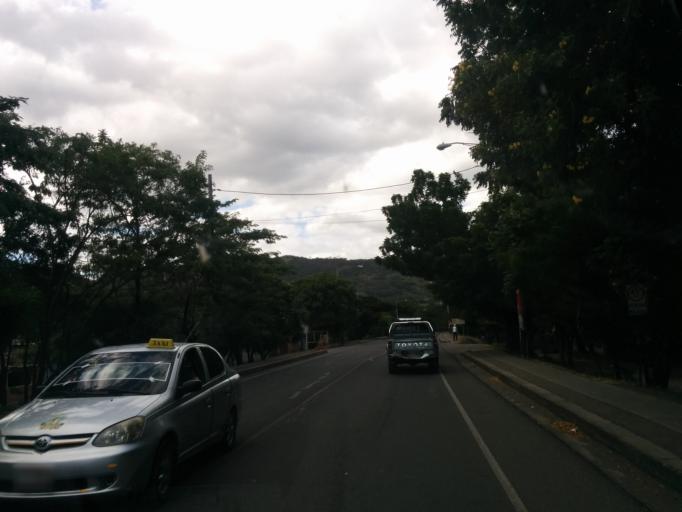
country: NI
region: Esteli
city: Esteli
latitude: 12.9618
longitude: -86.2307
